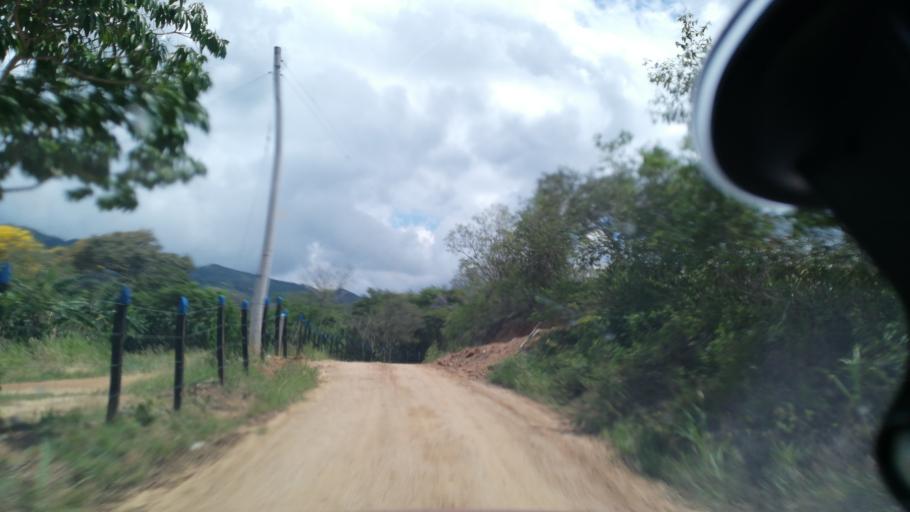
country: CO
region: Cundinamarca
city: Quipile
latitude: 4.7975
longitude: -74.6199
